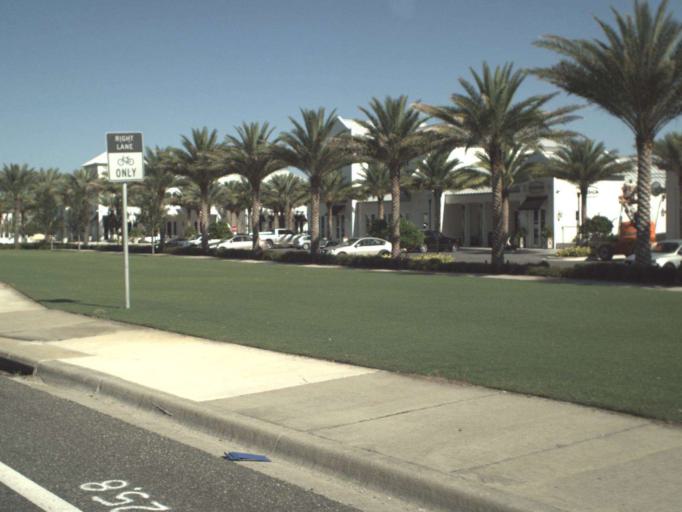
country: US
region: Florida
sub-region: Bay County
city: Laguna Beach
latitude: 30.2798
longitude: -86.0097
